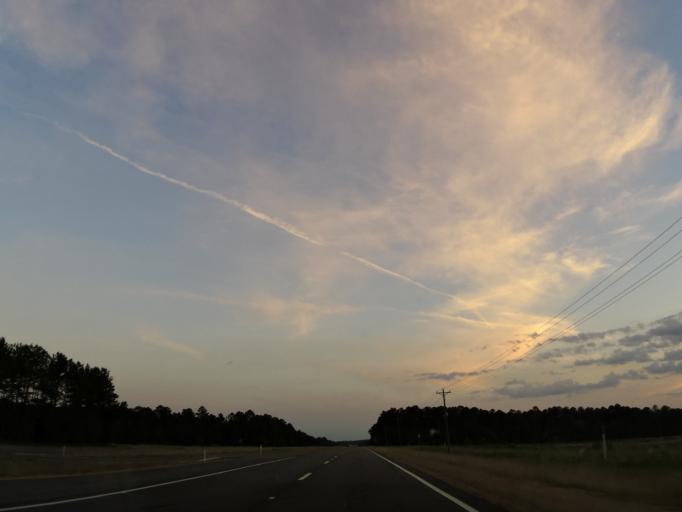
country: US
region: Mississippi
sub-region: Kemper County
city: De Kalb
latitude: 32.7155
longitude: -88.4802
